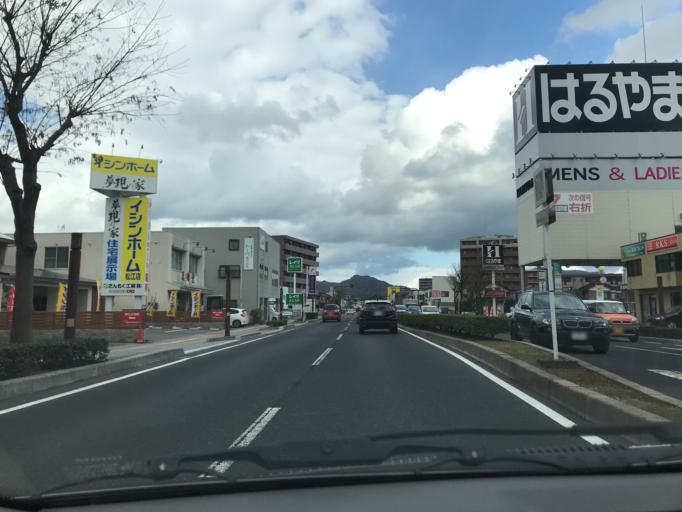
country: JP
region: Shimane
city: Matsue-shi
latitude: 35.4732
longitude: 133.0645
